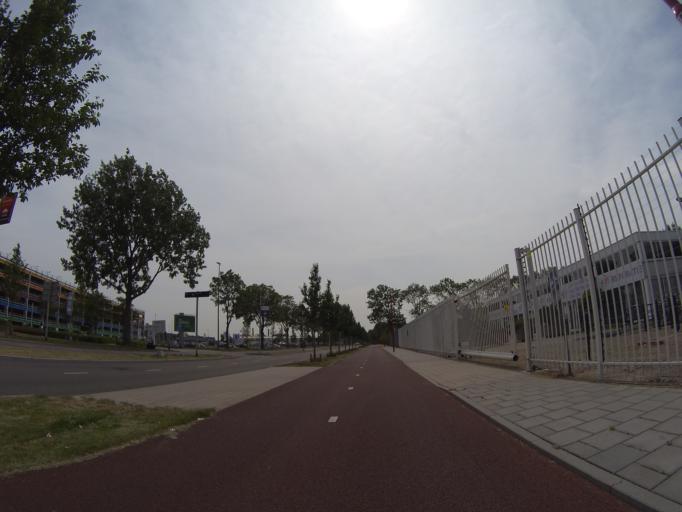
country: NL
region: Utrecht
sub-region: Gemeente Utrecht
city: Utrecht
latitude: 52.0830
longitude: 5.0990
